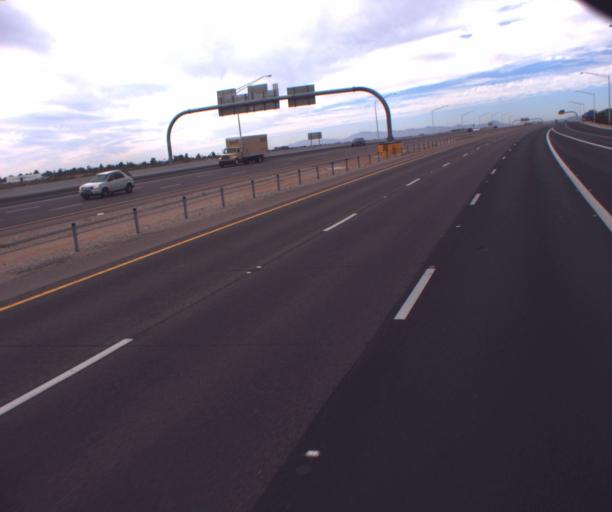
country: US
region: Arizona
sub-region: Maricopa County
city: Queen Creek
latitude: 33.3285
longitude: -111.6654
